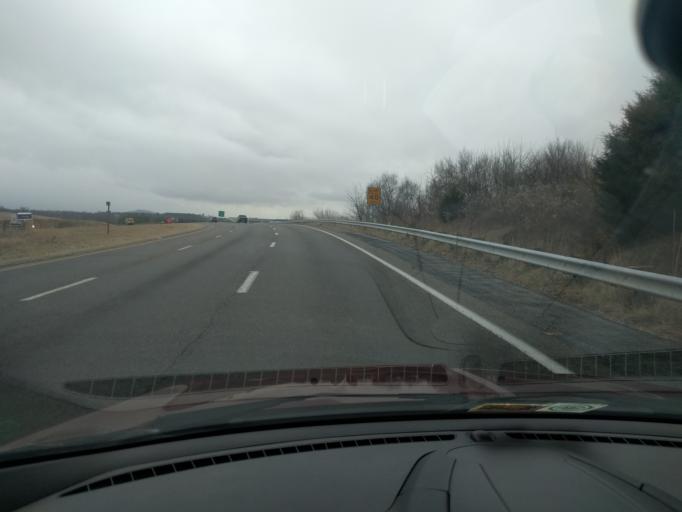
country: US
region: Virginia
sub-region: Augusta County
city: Jolivue
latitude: 38.1108
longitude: -79.0638
